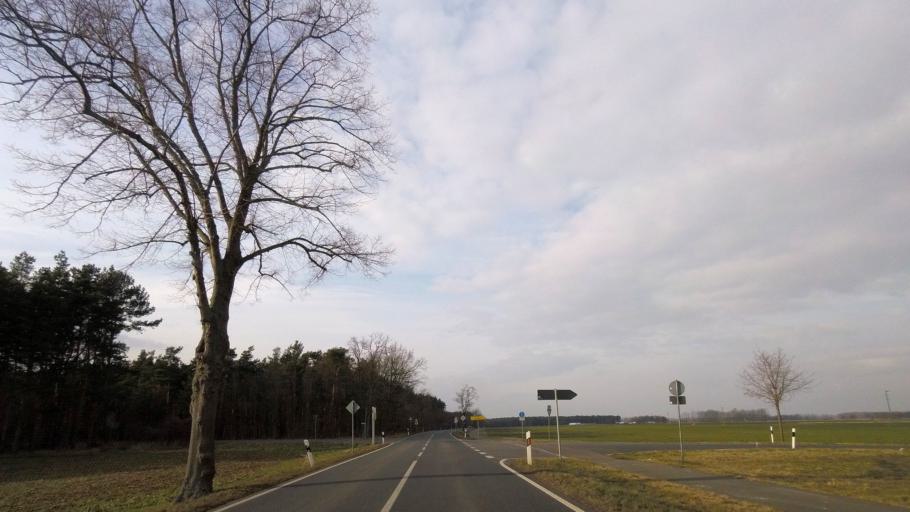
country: DE
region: Brandenburg
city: Belzig
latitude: 52.1854
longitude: 12.6181
